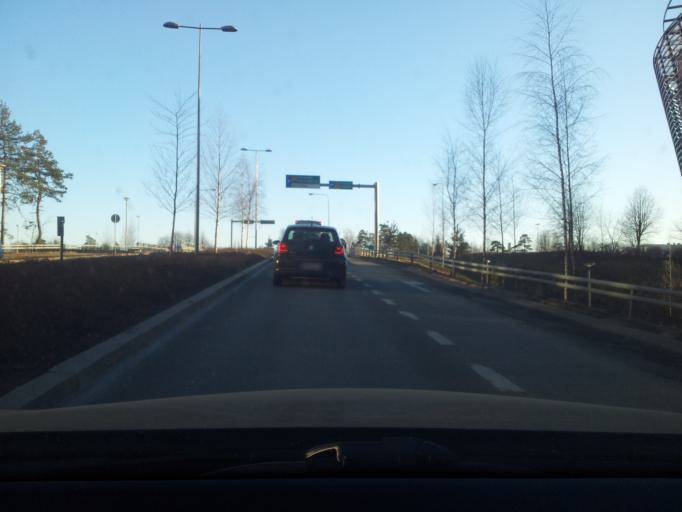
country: FI
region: Uusimaa
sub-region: Helsinki
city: Otaniemi
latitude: 60.1705
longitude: 24.8023
